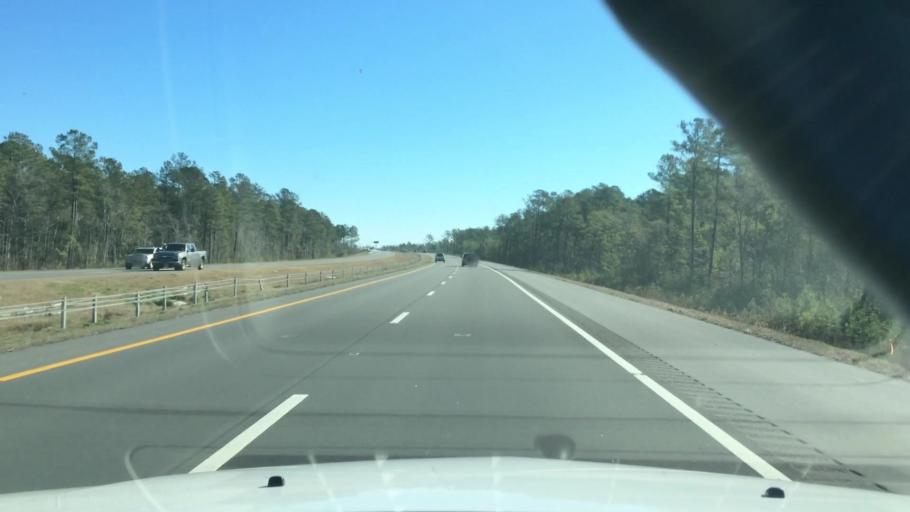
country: US
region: North Carolina
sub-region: Brunswick County
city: Leland
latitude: 34.2732
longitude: -78.0300
